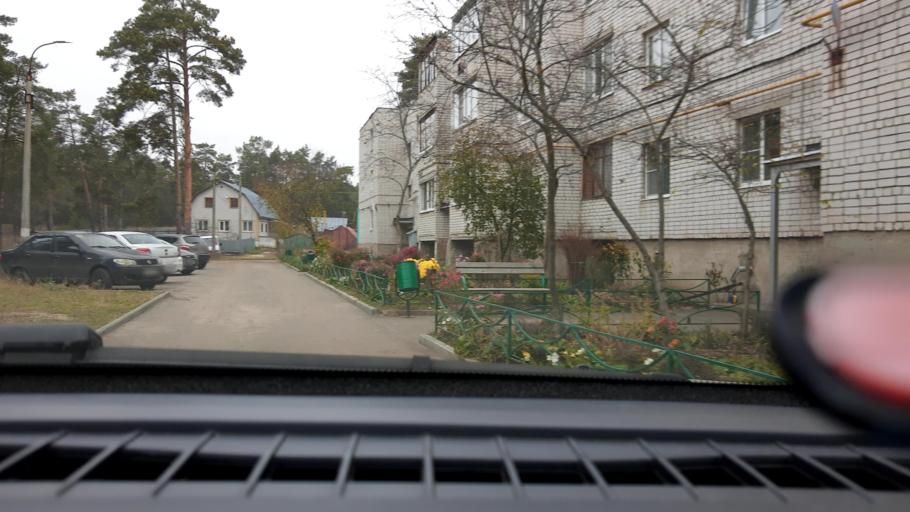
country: RU
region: Nizjnij Novgorod
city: Lukino
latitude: 56.3943
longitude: 43.7218
